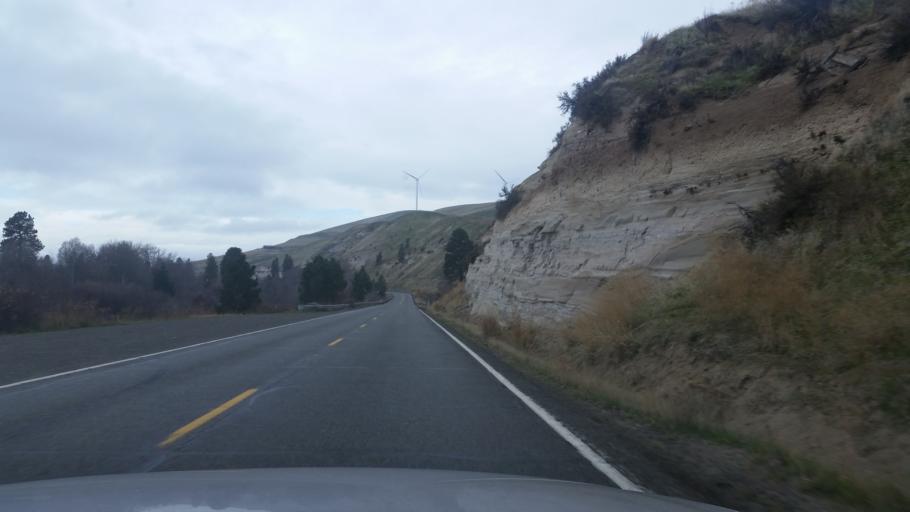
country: US
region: Washington
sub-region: Kittitas County
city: Ellensburg
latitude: 47.0964
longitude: -120.6889
